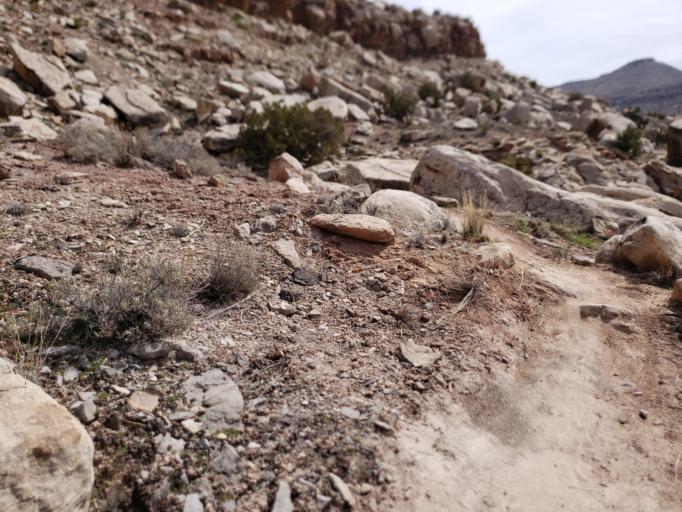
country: US
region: Colorado
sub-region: Mesa County
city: Loma
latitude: 39.1937
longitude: -108.8825
